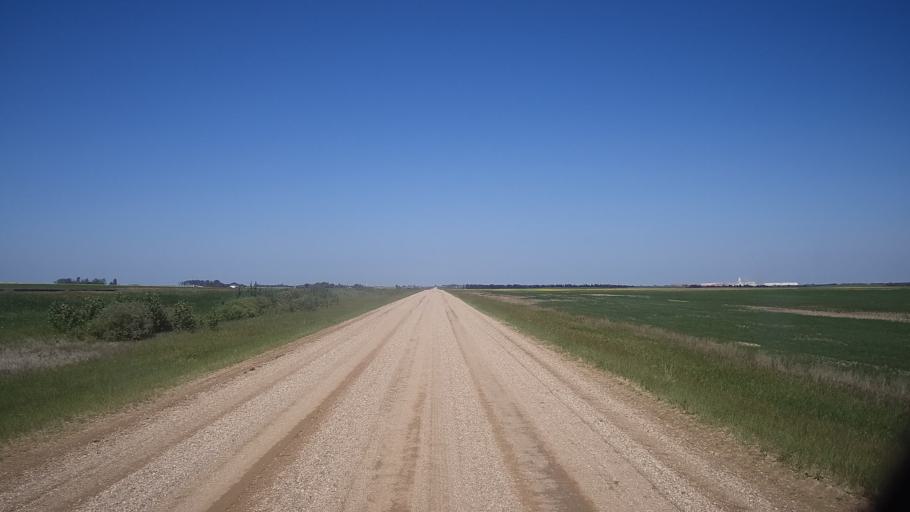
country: CA
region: Saskatchewan
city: Watrous
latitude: 51.8697
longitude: -105.9898
